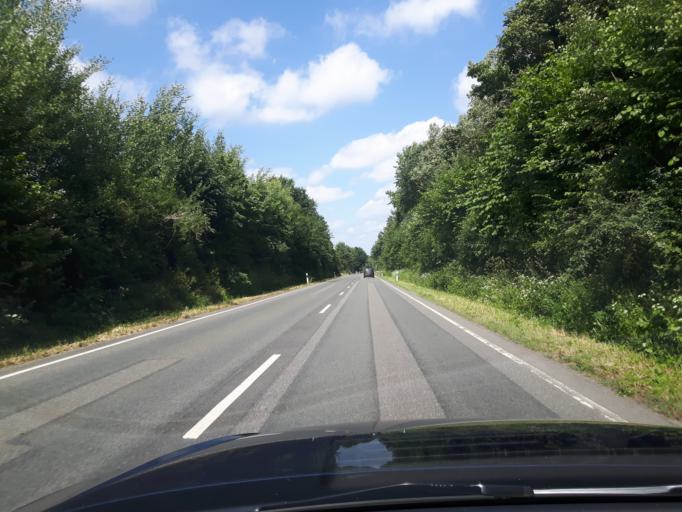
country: DE
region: Schleswig-Holstein
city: Scharbeutz
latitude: 54.0558
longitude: 10.7438
